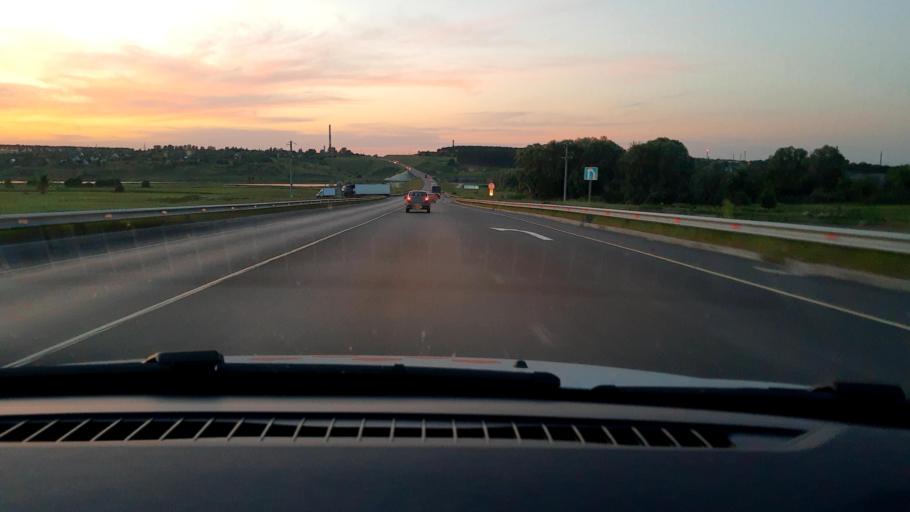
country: RU
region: Nizjnij Novgorod
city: Kstovo
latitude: 56.0701
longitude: 44.1310
